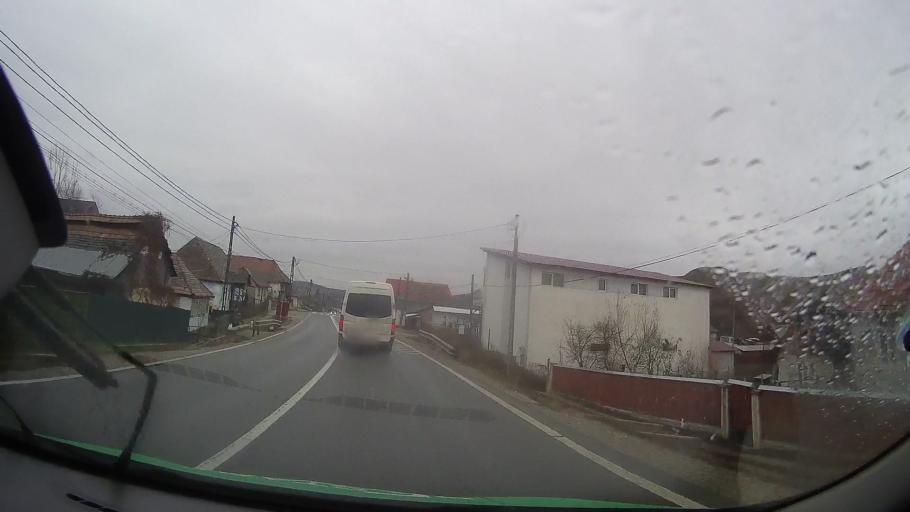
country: RO
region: Bistrita-Nasaud
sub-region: Comuna Galatii Bistritei
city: Galatii Bistritei
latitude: 47.0191
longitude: 24.4137
